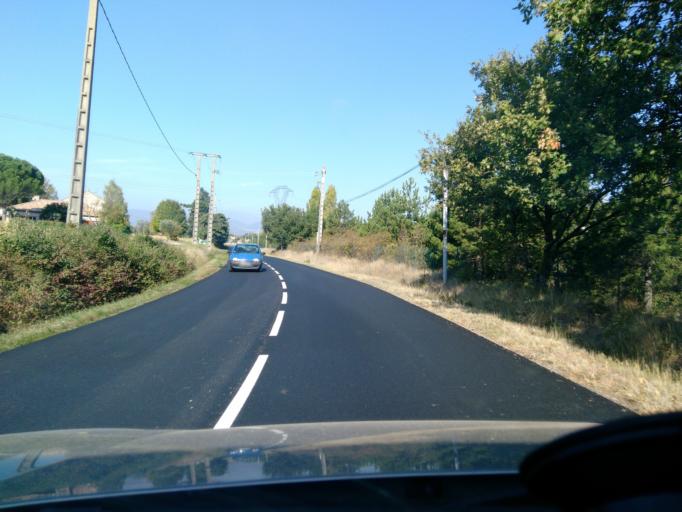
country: FR
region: Rhone-Alpes
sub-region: Departement de la Drome
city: Montboucher-sur-Jabron
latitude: 44.5393
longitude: 4.7978
